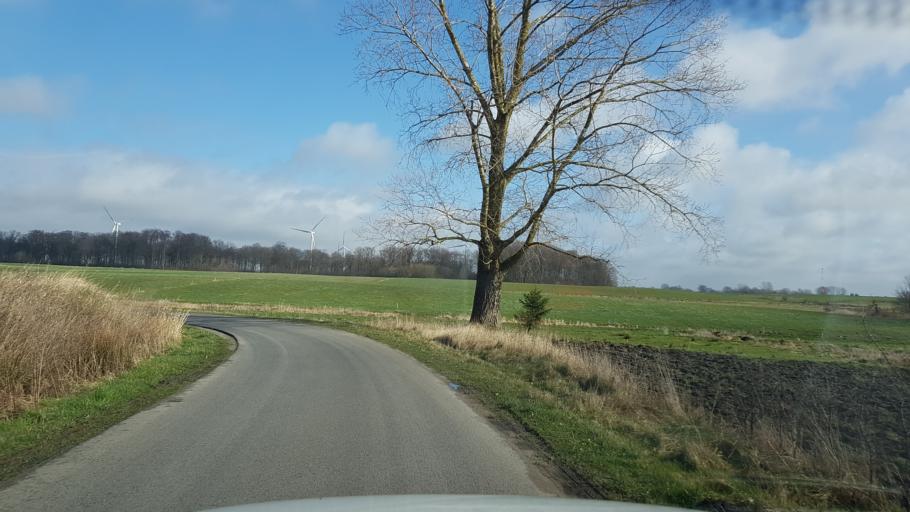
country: PL
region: West Pomeranian Voivodeship
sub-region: Powiat slawienski
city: Slawno
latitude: 54.4817
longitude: 16.6528
